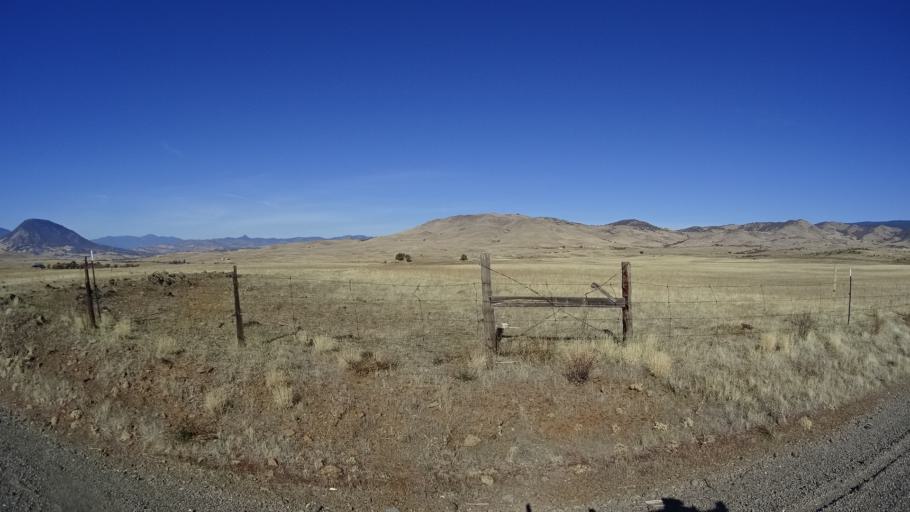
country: US
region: California
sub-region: Siskiyou County
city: Montague
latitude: 41.8045
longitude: -122.4025
